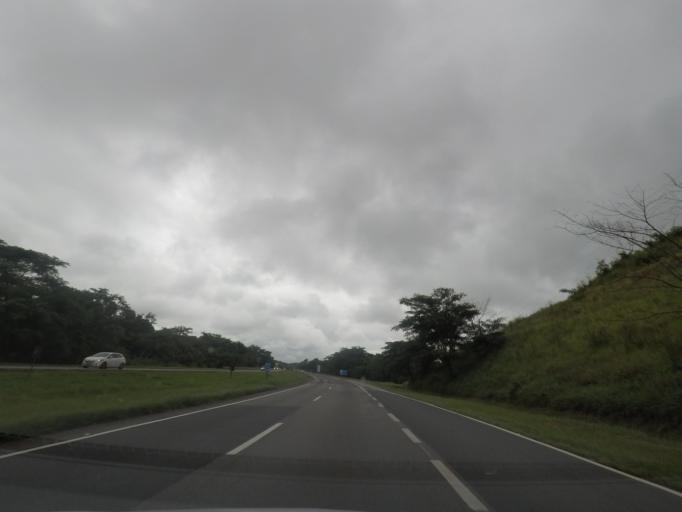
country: BR
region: Sao Paulo
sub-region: Registro
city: Registro
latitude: -24.5980
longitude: -47.8760
